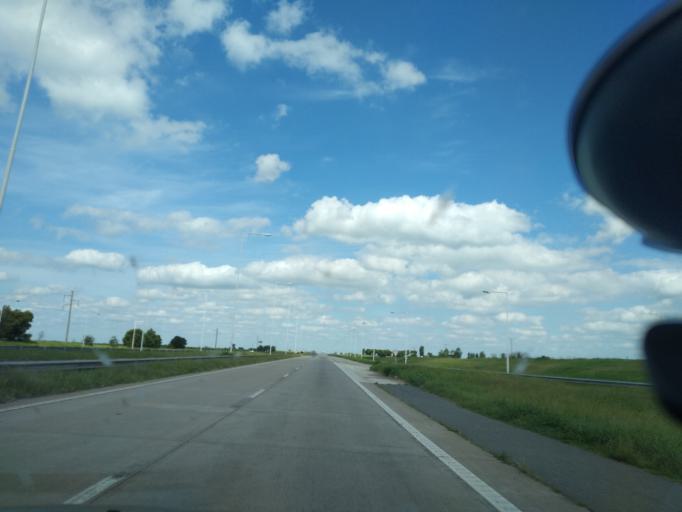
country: AR
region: Santa Fe
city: Canada de Gomez
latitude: -32.8558
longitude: -61.3378
